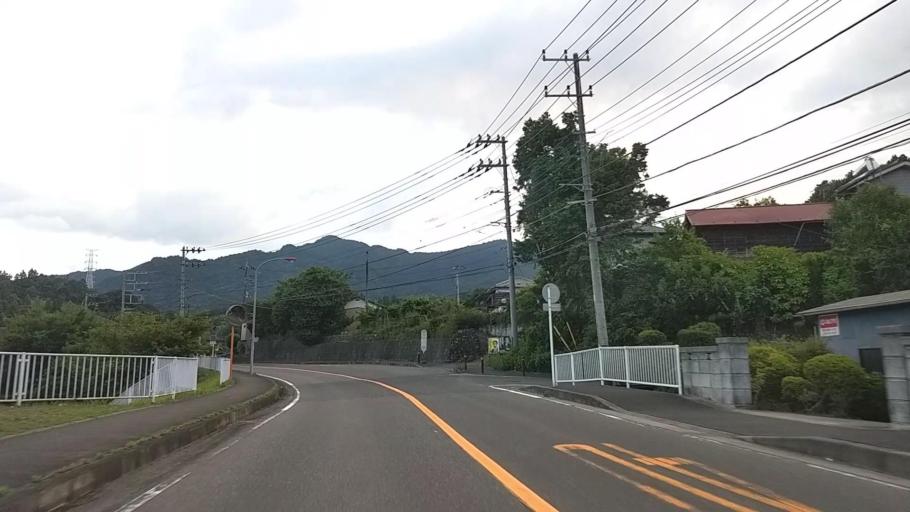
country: JP
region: Yamanashi
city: Uenohara
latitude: 35.6023
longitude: 139.2175
